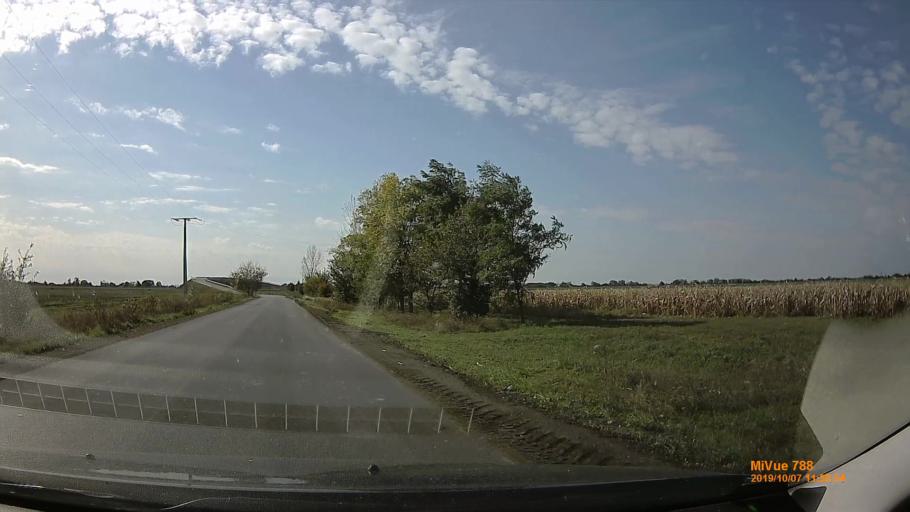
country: HU
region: Bekes
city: Kondoros
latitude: 46.7912
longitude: 20.7139
